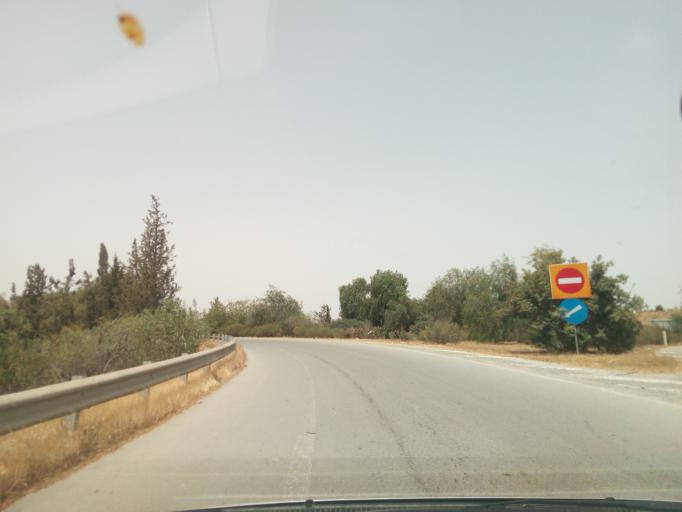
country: CY
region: Larnaka
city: Aradippou
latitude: 34.9616
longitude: 33.5855
